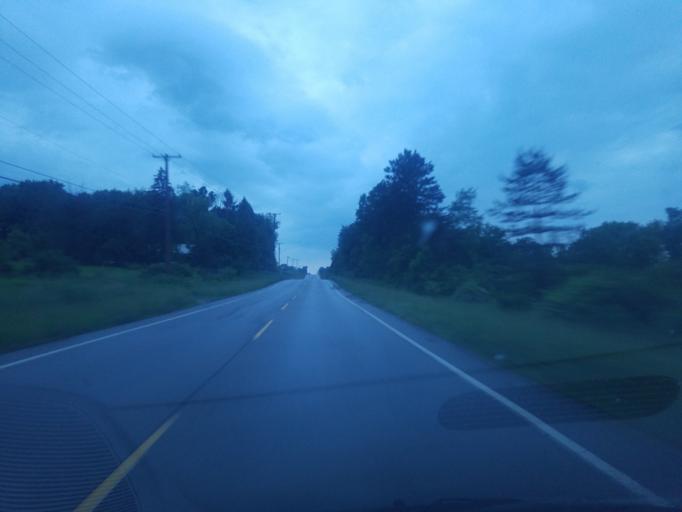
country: US
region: Ohio
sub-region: Mahoning County
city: Canfield
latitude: 40.9881
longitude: -80.7306
